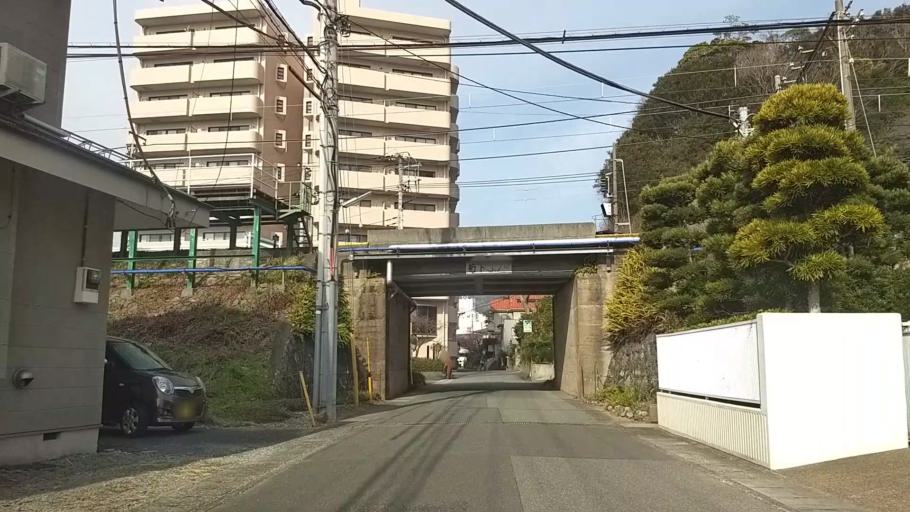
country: JP
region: Shizuoka
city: Shimoda
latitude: 34.7482
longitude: 138.9971
